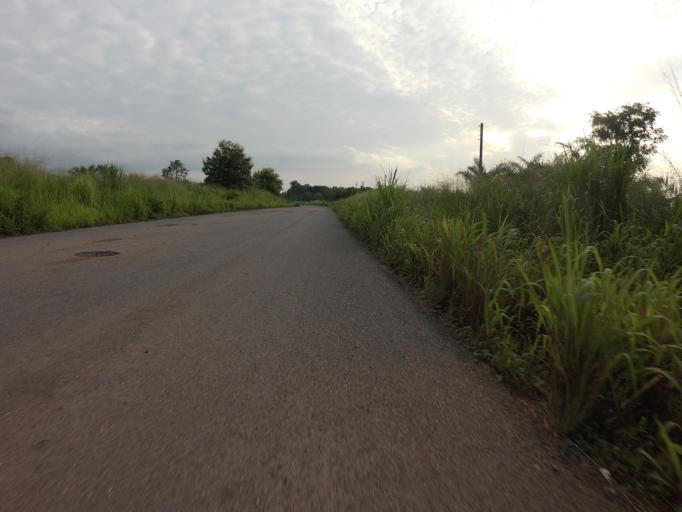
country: GH
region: Volta
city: Kpandu
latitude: 6.8671
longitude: 0.4047
